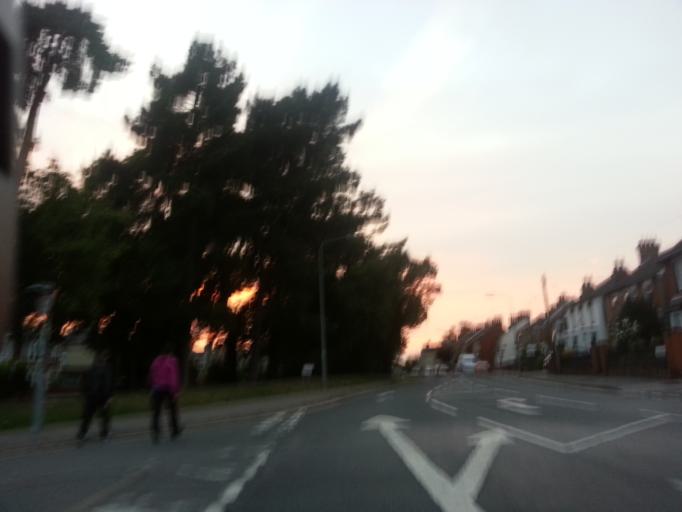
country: GB
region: England
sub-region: Suffolk
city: Ipswich
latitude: 52.0451
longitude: 1.1797
